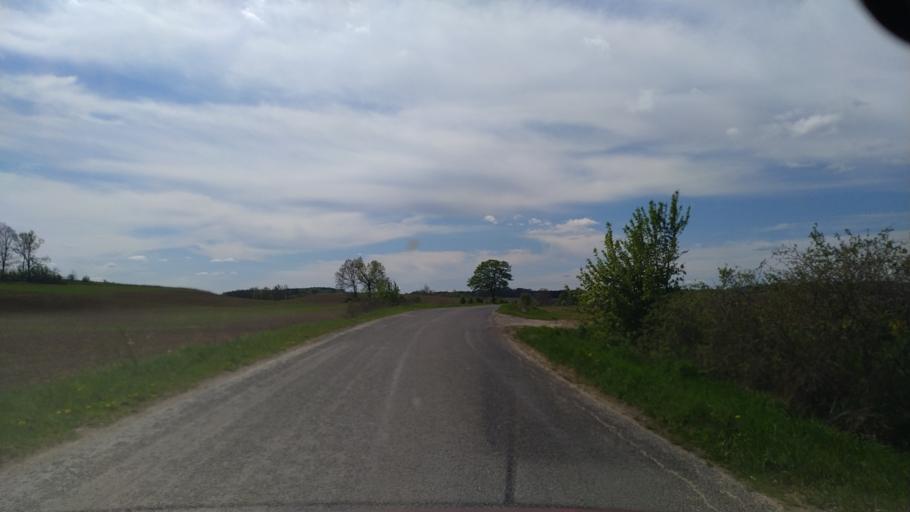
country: PL
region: West Pomeranian Voivodeship
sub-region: Powiat walecki
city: Walcz
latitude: 53.3536
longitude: 16.3171
